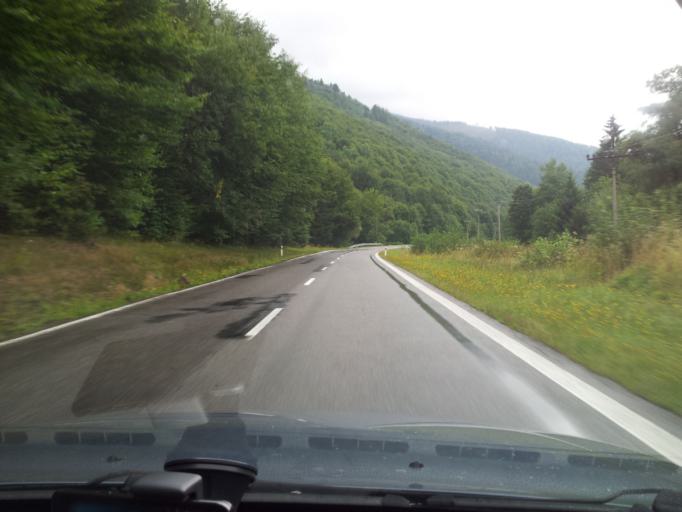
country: SK
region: Banskobystricky
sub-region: Okres Banska Bystrica
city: Brezno
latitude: 48.8776
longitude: 19.6559
